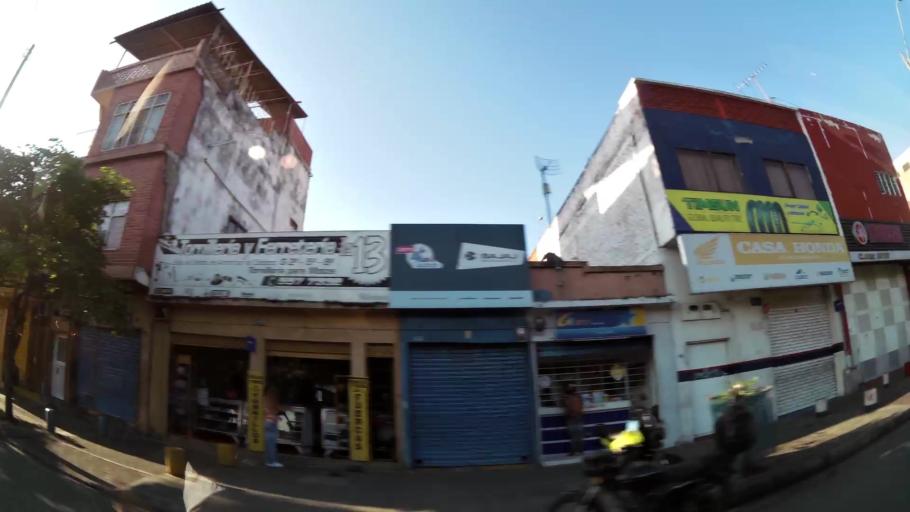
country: CO
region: Valle del Cauca
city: Cali
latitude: 3.4426
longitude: -76.5279
